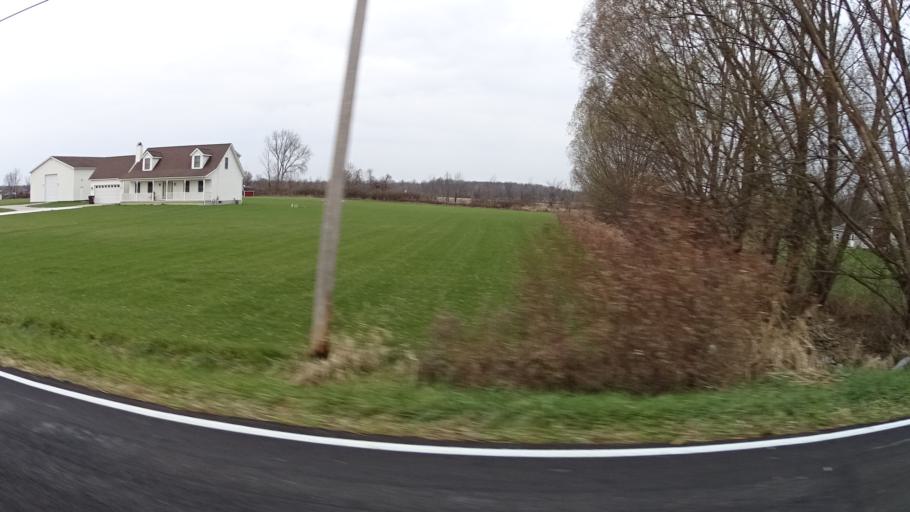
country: US
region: Ohio
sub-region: Lorain County
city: Lagrange
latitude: 41.1730
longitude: -82.0835
